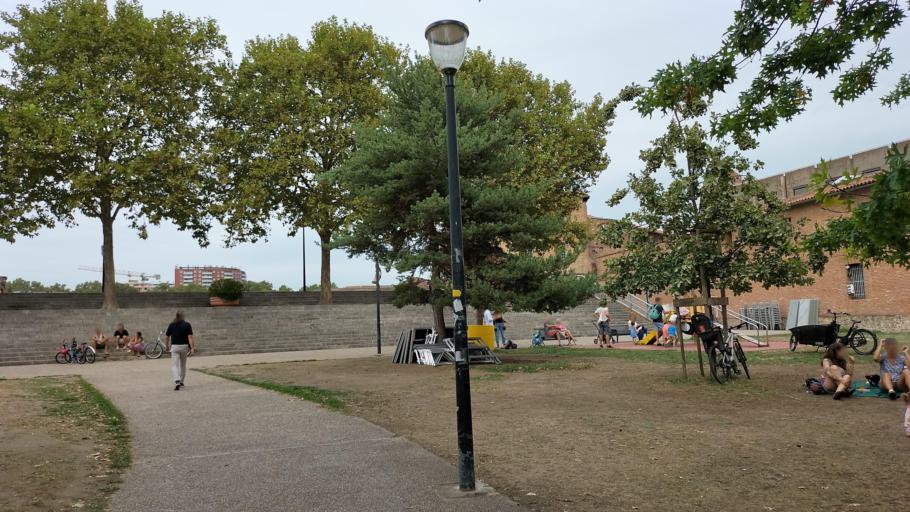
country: FR
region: Midi-Pyrenees
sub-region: Departement de la Haute-Garonne
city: Toulouse
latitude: 43.6010
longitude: 1.4310
